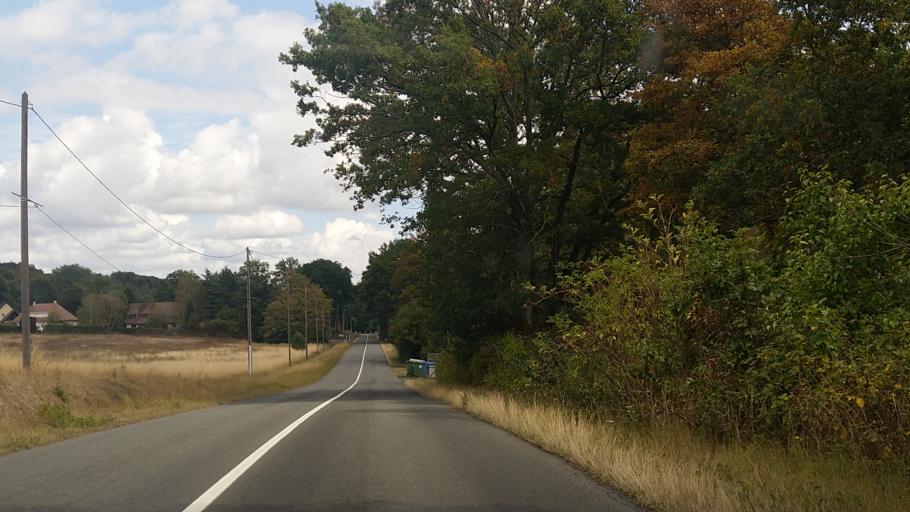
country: FR
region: Ile-de-France
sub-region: Departement des Yvelines
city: Sonchamp
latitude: 48.5690
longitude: 1.8966
